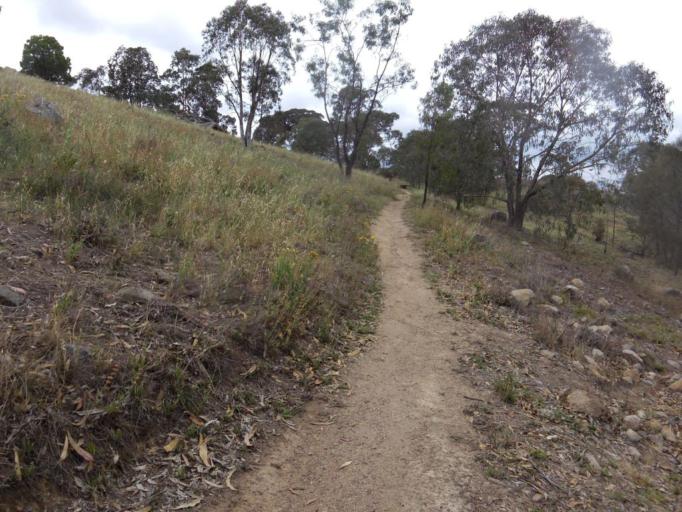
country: AU
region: Australian Capital Territory
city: Forrest
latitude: -35.3578
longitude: 149.0300
